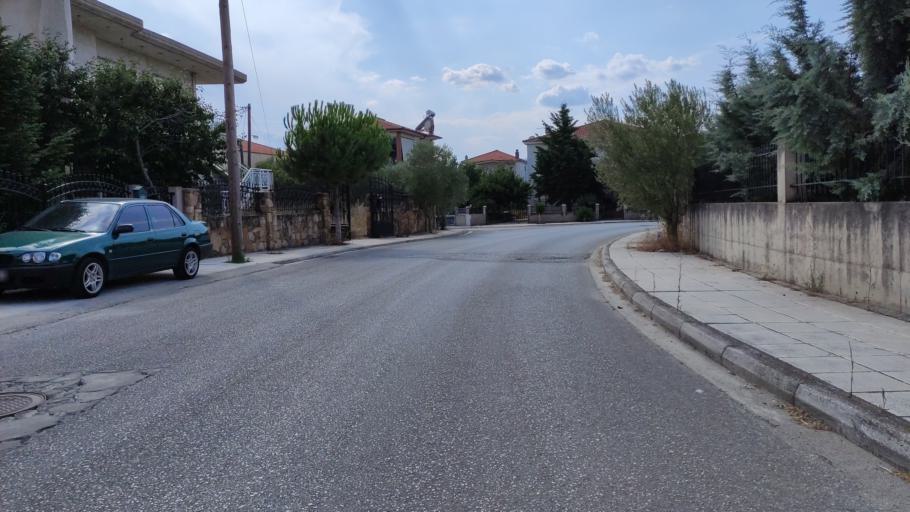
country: GR
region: East Macedonia and Thrace
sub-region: Nomos Rodopis
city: Komotini
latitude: 41.1316
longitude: 25.4003
